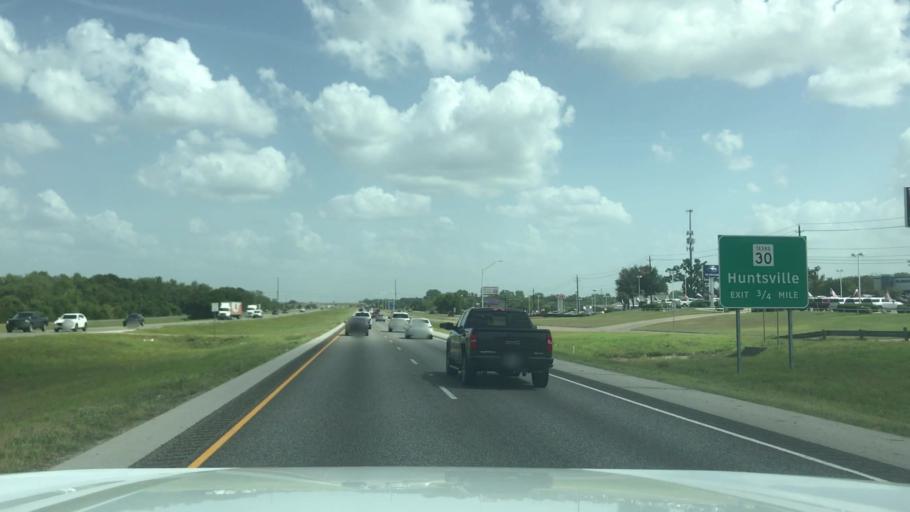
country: US
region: Texas
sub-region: Brazos County
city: College Station
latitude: 30.6512
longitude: -96.3186
